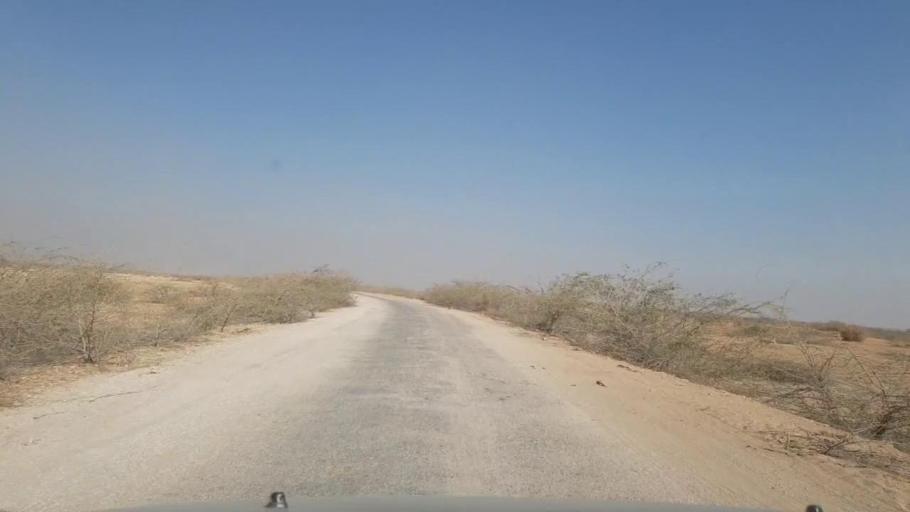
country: PK
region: Sindh
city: Thatta
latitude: 24.8480
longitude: 67.8932
